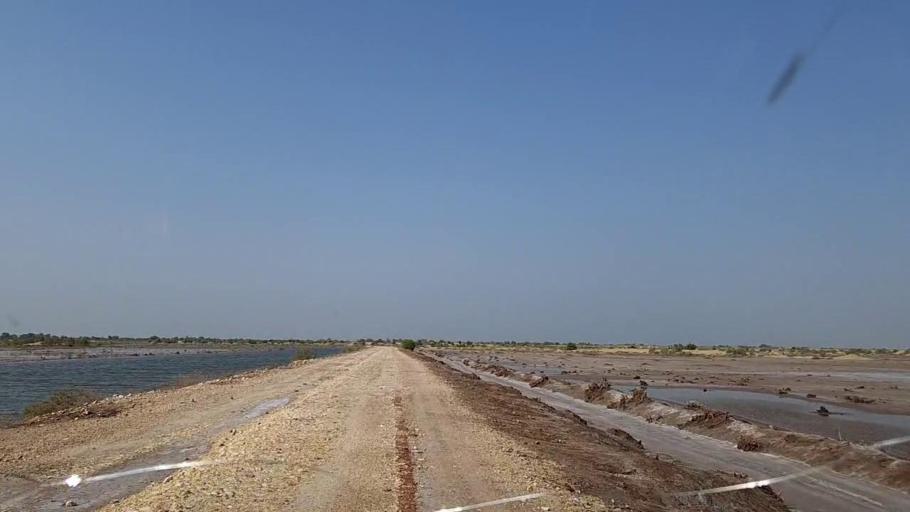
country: PK
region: Sindh
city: Khanpur
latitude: 27.6921
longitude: 69.3830
